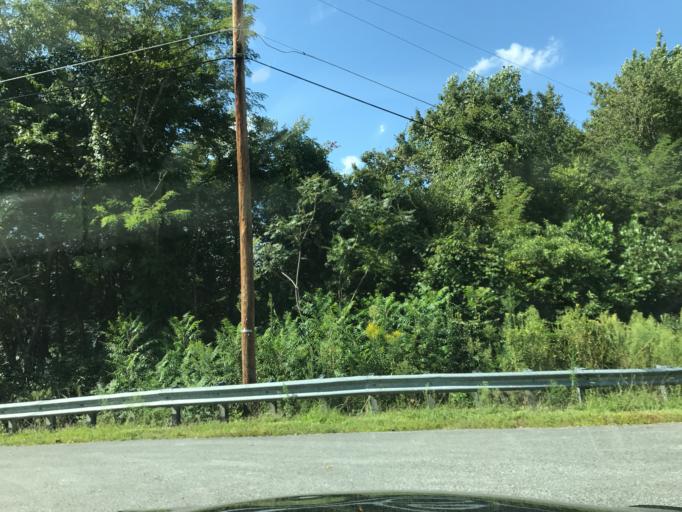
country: US
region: Pennsylvania
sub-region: York County
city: New Freedom
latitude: 39.6353
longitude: -76.6675
